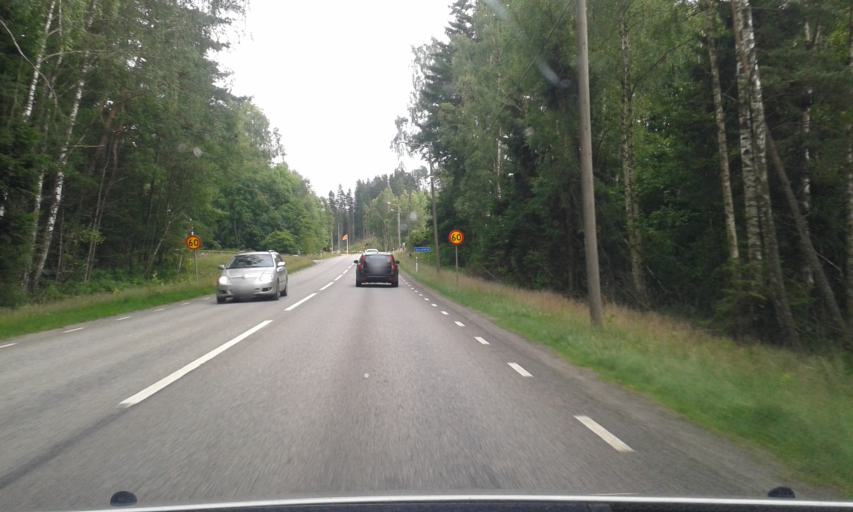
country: SE
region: Halland
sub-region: Varbergs Kommun
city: Tvaaker
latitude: 57.1407
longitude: 12.6975
